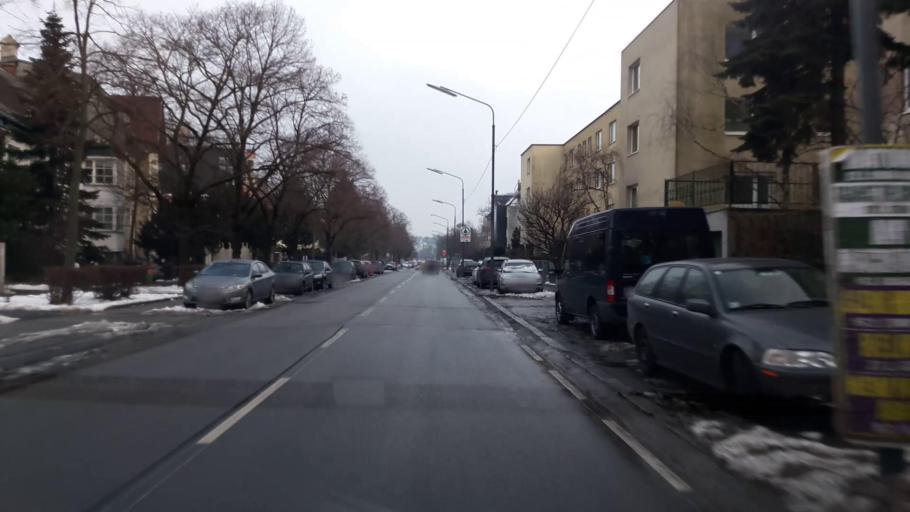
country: AT
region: Lower Austria
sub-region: Politischer Bezirk Wien-Umgebung
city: Klosterneuburg
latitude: 48.2472
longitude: 16.3131
